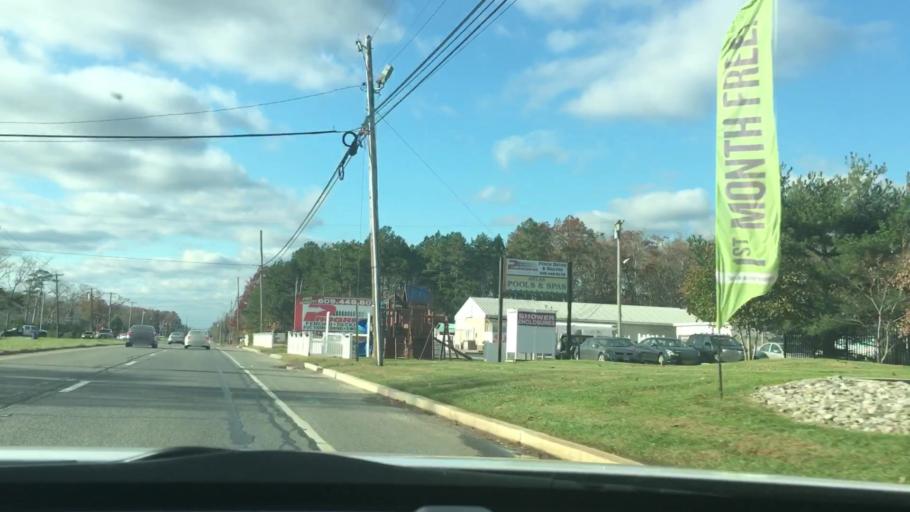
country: US
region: New Jersey
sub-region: Atlantic County
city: Pomona
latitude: 39.4202
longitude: -74.5854
